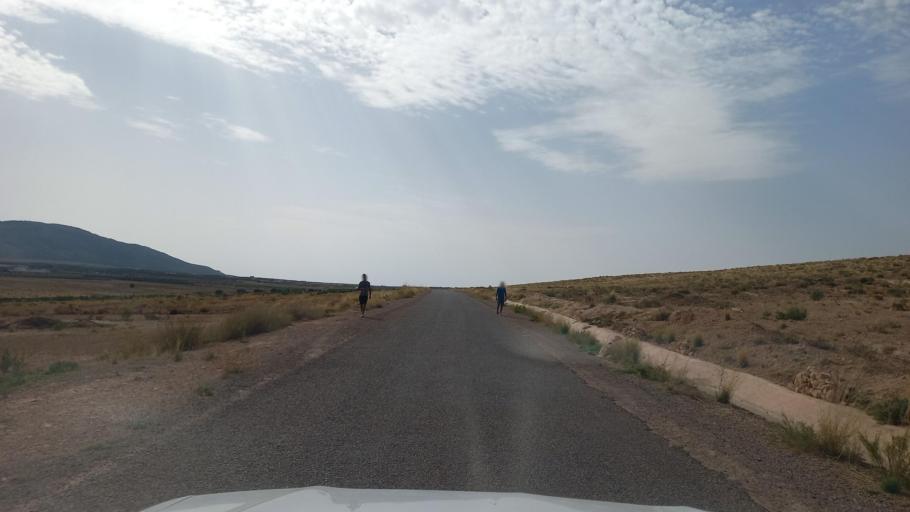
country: TN
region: Al Qasrayn
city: Kasserine
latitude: 35.3605
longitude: 8.8396
